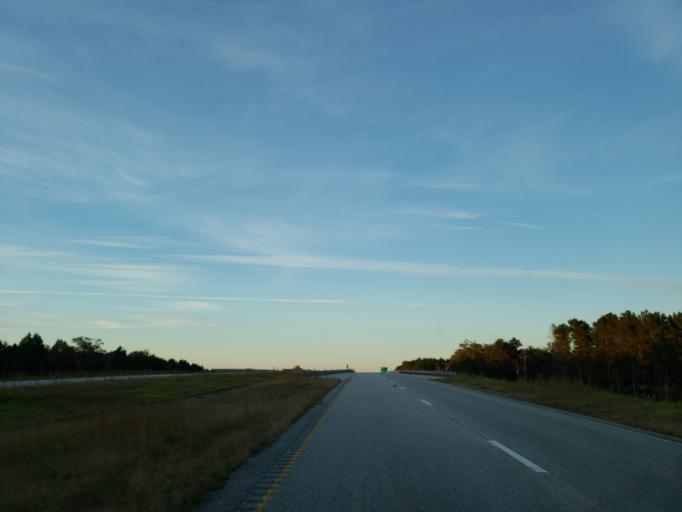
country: US
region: Mississippi
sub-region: Wayne County
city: Belmont
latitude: 31.4439
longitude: -88.4652
